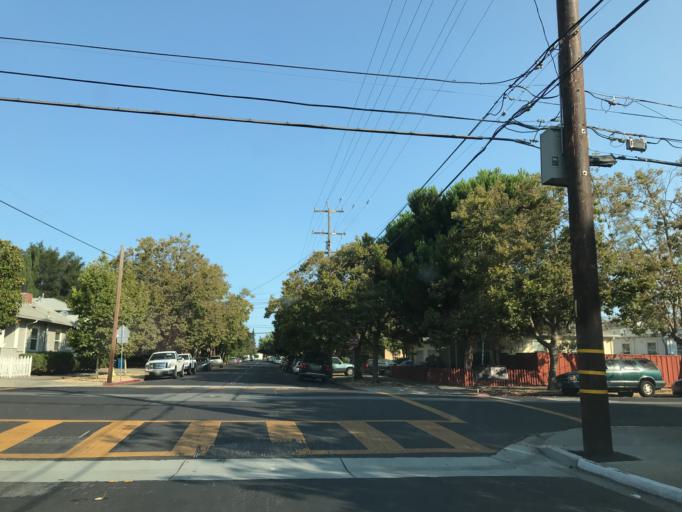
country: US
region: California
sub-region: San Mateo County
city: Redwood City
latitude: 37.4899
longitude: -122.2348
